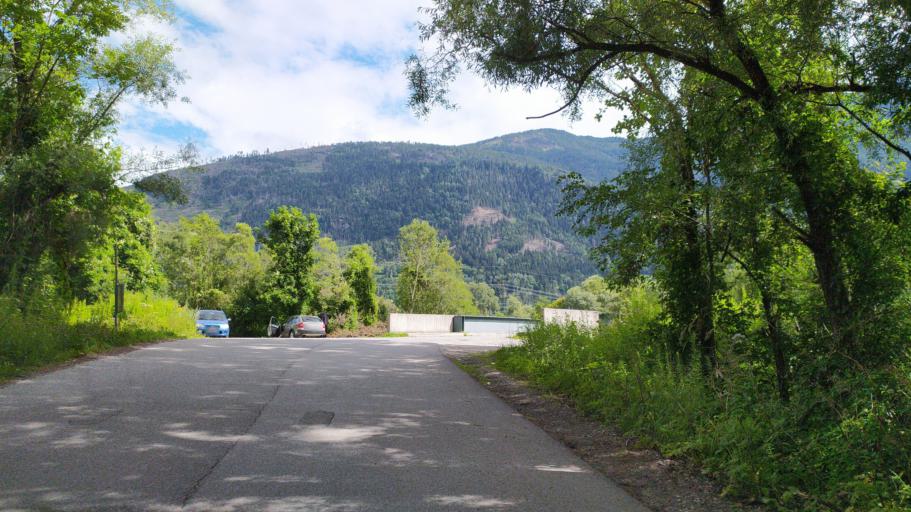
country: AT
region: Tyrol
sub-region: Politischer Bezirk Lienz
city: Lavant
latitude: 46.7899
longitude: 12.8741
